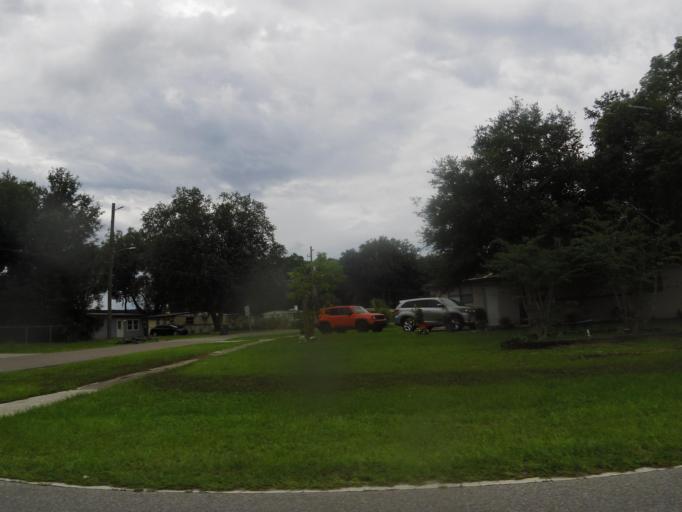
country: US
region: Florida
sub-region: Duval County
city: Jacksonville
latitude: 30.3212
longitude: -81.5334
